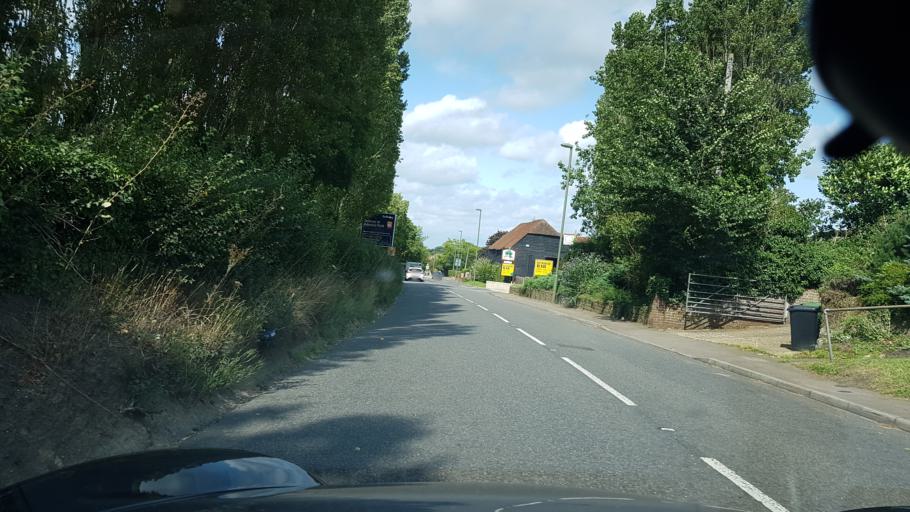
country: GB
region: England
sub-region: Surrey
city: Seale
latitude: 51.2280
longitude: -0.7330
